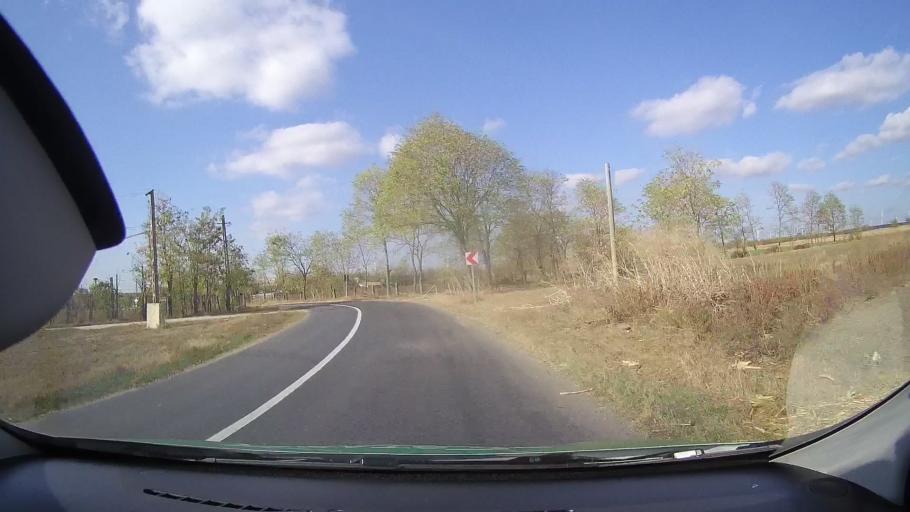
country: RO
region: Constanta
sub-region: Comuna Cogealac
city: Tariverde
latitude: 44.5635
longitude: 28.6047
